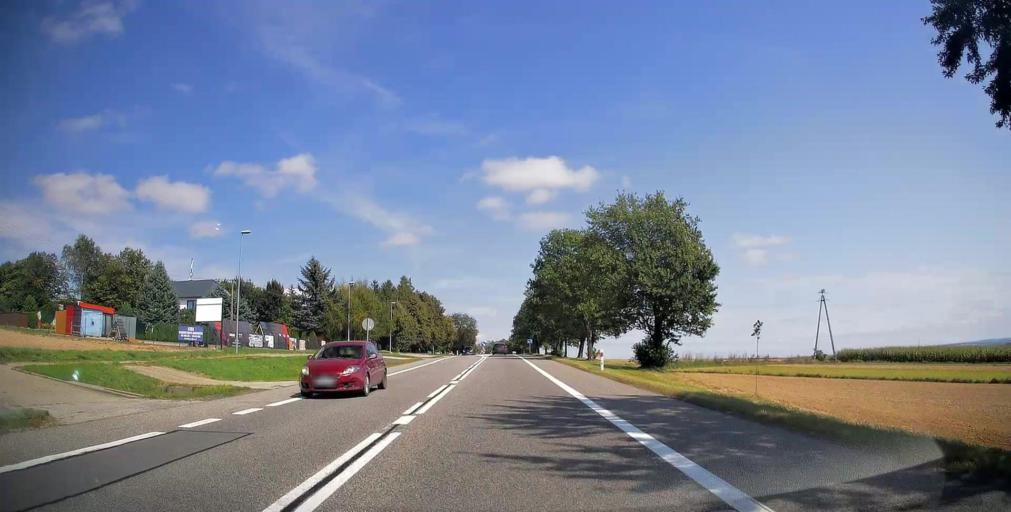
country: PL
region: Lesser Poland Voivodeship
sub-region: Powiat miechowski
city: Miechow
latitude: 50.4045
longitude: 20.1025
